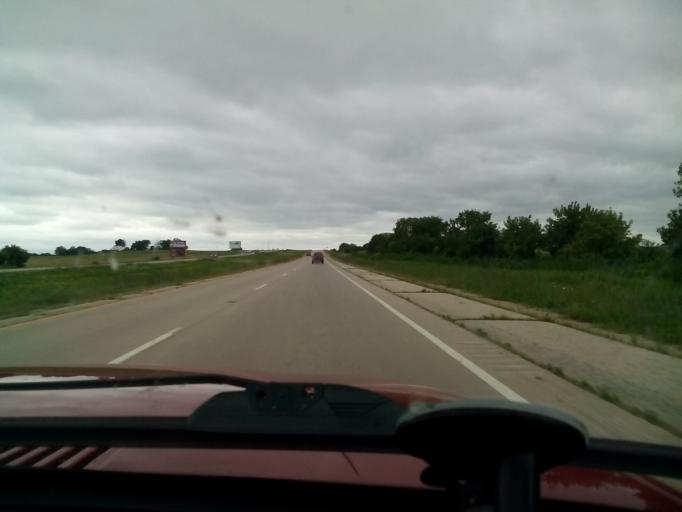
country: US
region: Wisconsin
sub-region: Columbia County
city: Columbus
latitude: 43.2960
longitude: -89.0636
